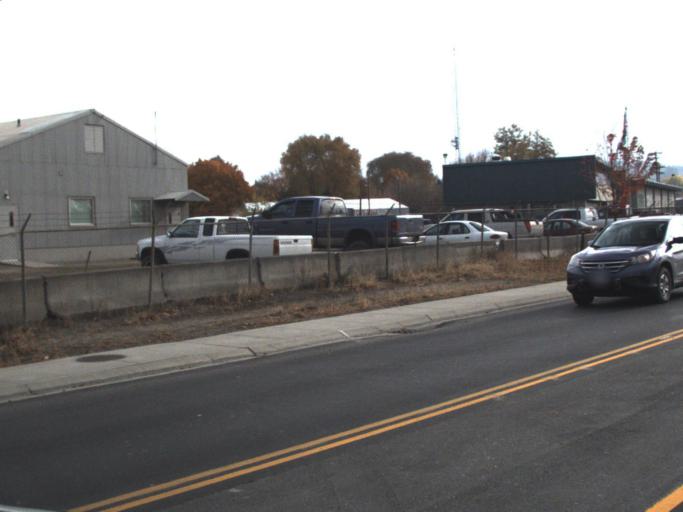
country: US
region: Washington
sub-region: Stevens County
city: Colville
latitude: 48.5499
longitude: -117.9129
